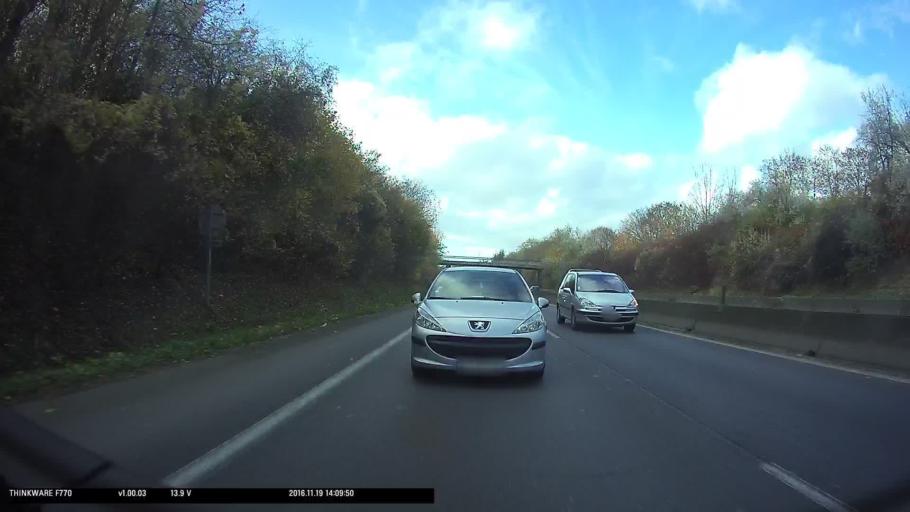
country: FR
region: Ile-de-France
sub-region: Departement du Val-d'Oise
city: Osny
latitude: 49.0522
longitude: 2.0641
